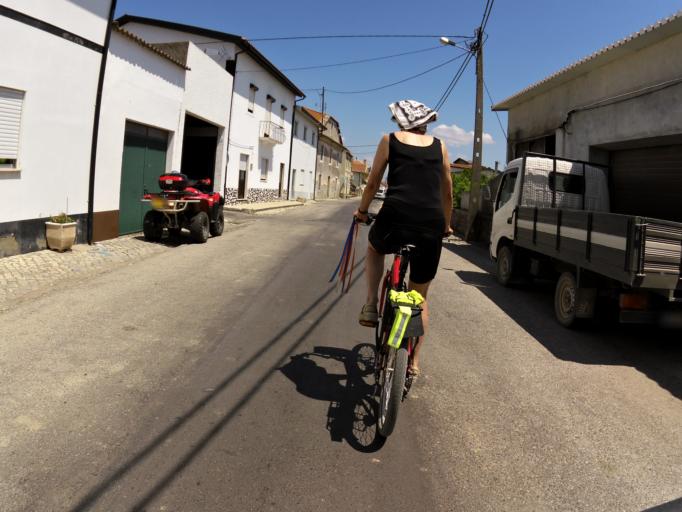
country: PT
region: Coimbra
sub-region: Montemor-O-Velho
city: Montemor-o-Velho
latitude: 40.1505
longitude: -8.7110
